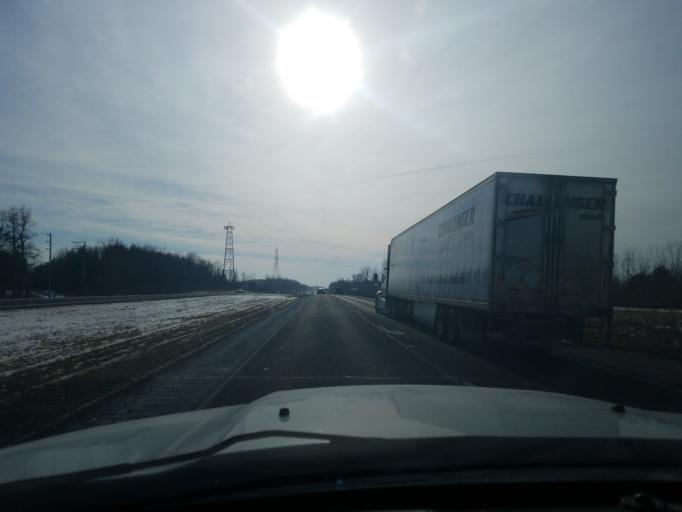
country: US
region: Indiana
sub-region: Huntington County
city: Roanoke
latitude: 40.9493
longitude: -85.3004
